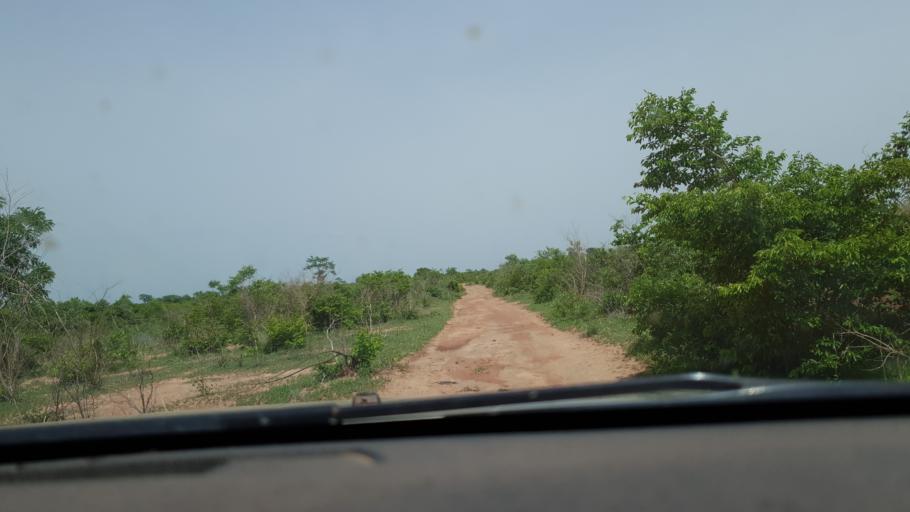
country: ML
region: Koulikoro
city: Koulikoro
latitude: 12.6652
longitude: -7.2232
